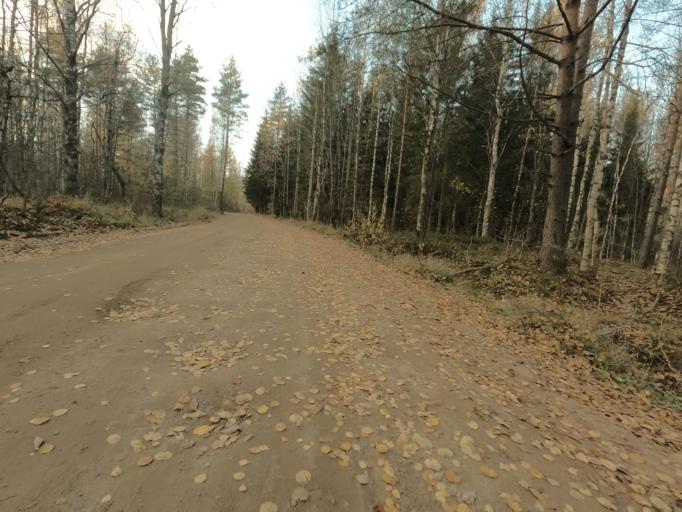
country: RU
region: Leningrad
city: Priladozhskiy
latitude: 59.7455
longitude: 31.3077
